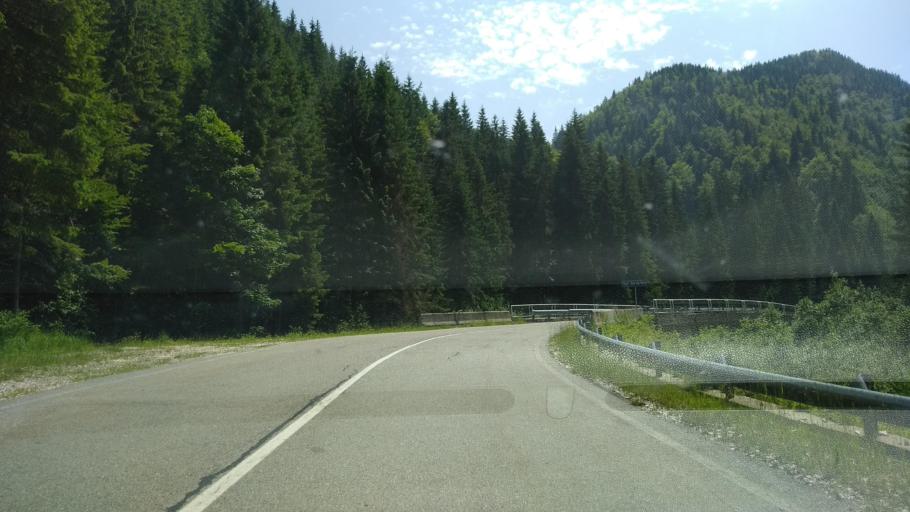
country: RO
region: Hunedoara
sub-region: Comuna Rau de Mori
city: Rau de Mori
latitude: 45.2728
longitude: 22.8954
